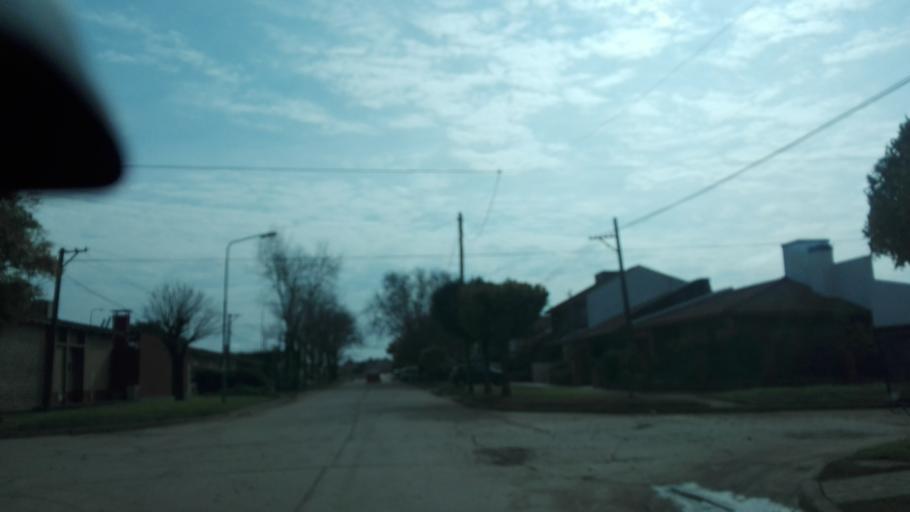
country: AR
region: Buenos Aires
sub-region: Partido de Chascomus
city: Chascomus
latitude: -35.5774
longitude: -58.0009
